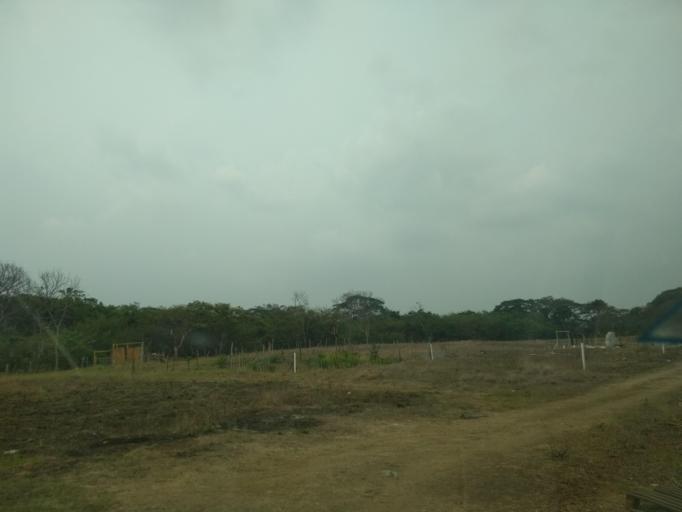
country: MX
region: Veracruz
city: Paso del Toro
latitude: 19.0260
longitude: -96.1449
